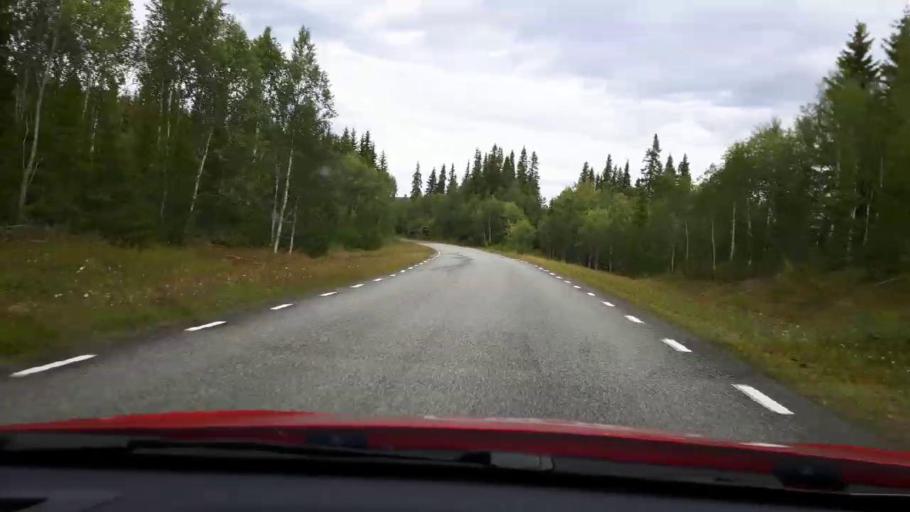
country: SE
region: Jaemtland
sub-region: Are Kommun
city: Are
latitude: 63.7173
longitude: 12.9669
